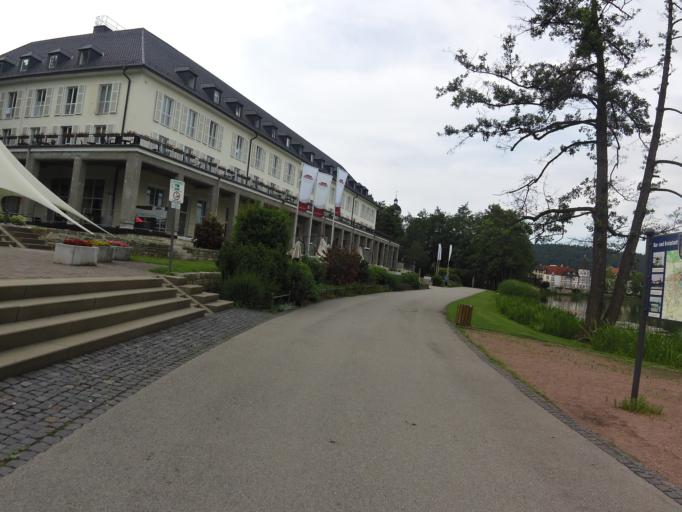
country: DE
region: Thuringia
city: Bad Salzungen
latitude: 50.8099
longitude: 10.2348
